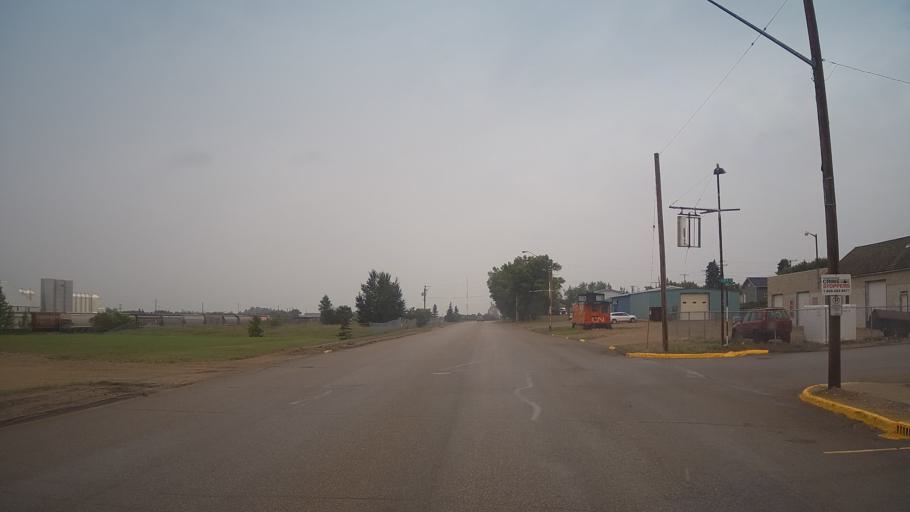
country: CA
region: Saskatchewan
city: Biggar
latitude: 52.0545
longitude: -107.9885
